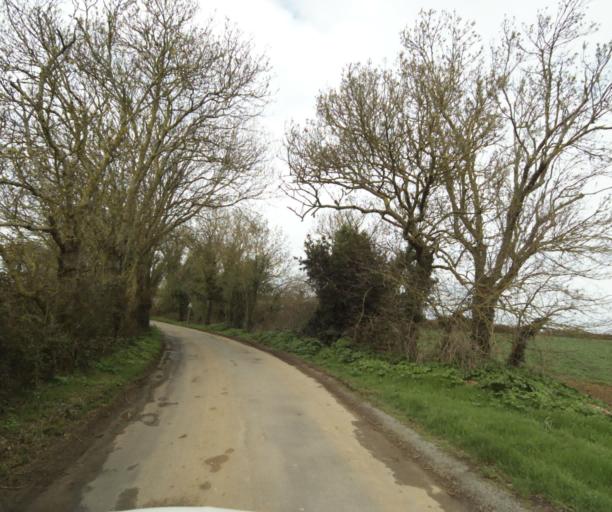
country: FR
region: Poitou-Charentes
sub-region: Departement de la Charente-Maritime
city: Nieul-sur-Mer
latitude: 46.1909
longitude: -1.1745
